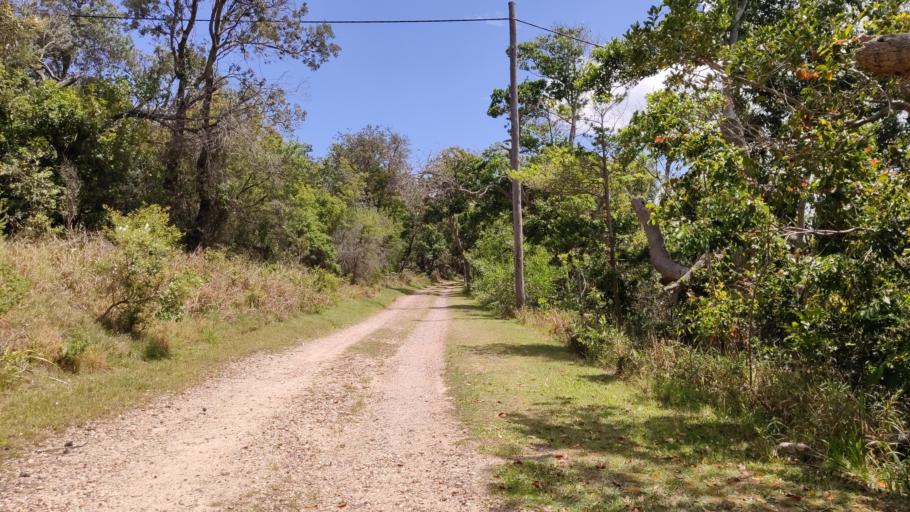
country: AU
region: New South Wales
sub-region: Port Macquarie-Hastings
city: North Haven
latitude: -31.6401
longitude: 152.8349
